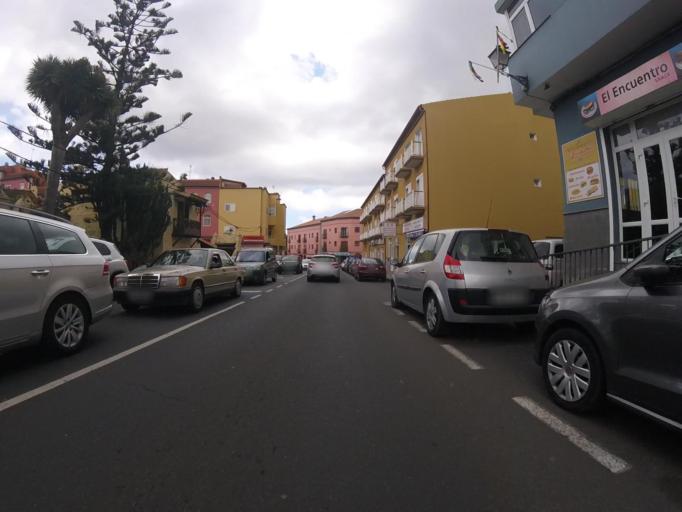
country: ES
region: Canary Islands
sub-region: Provincia de Las Palmas
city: Vega de San Mateo
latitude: 28.0105
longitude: -15.5307
